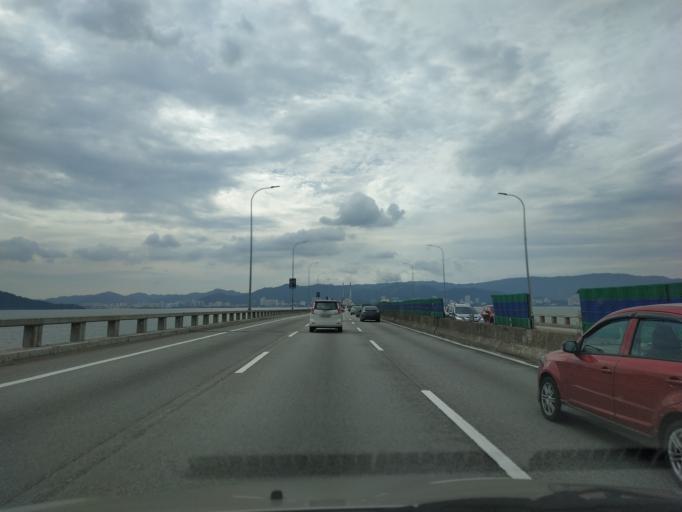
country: MY
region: Penang
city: Perai
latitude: 5.3514
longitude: 100.3636
